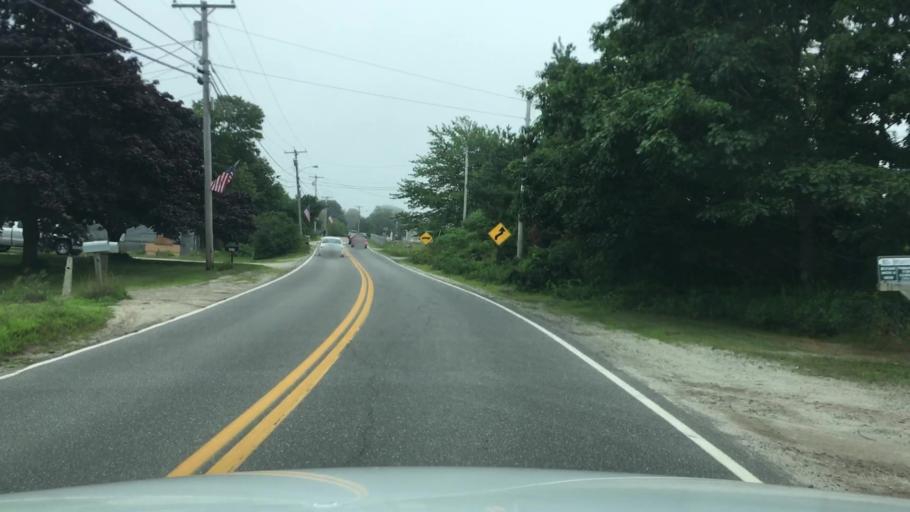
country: US
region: Maine
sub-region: Cumberland County
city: Harpswell Center
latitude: 43.7400
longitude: -69.9940
